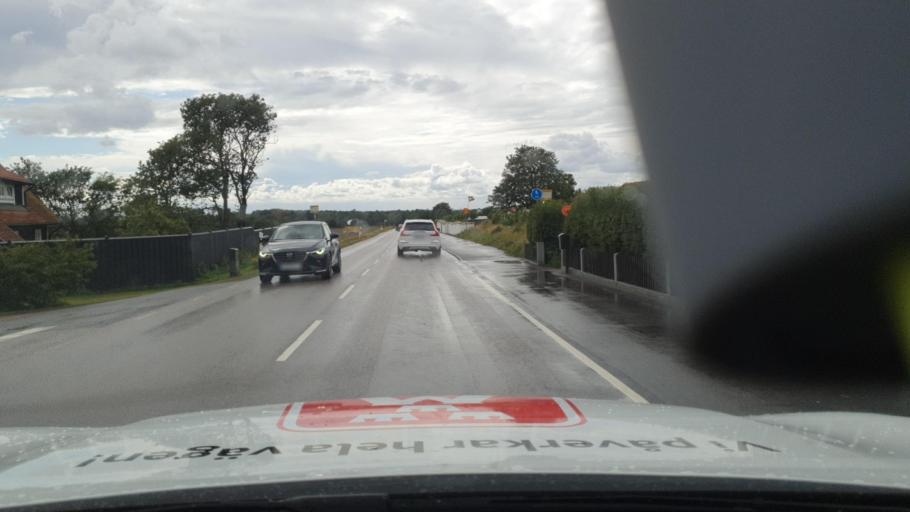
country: SE
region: Skane
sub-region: Angelholms Kommun
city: Vejbystrand
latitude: 56.4324
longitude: 12.6546
